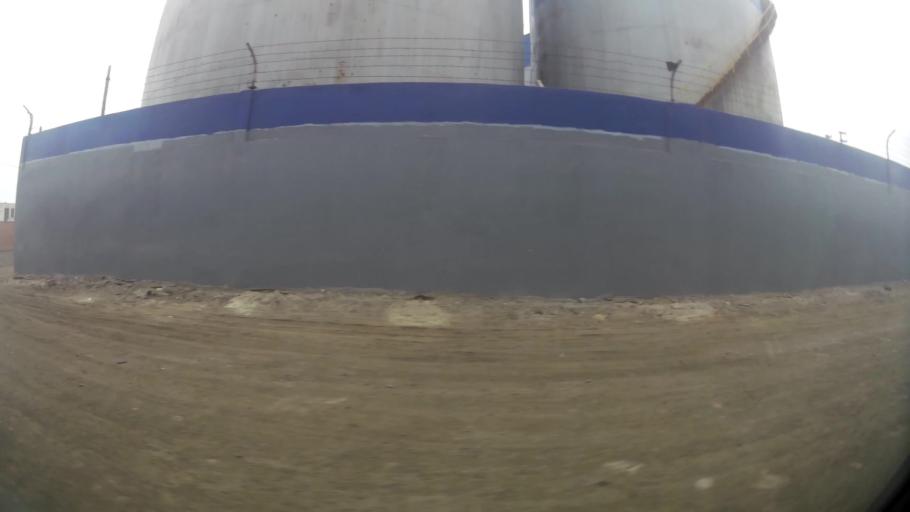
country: PE
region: Lima
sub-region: Provincia de Huaral
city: Chancay
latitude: -11.5760
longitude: -77.2698
